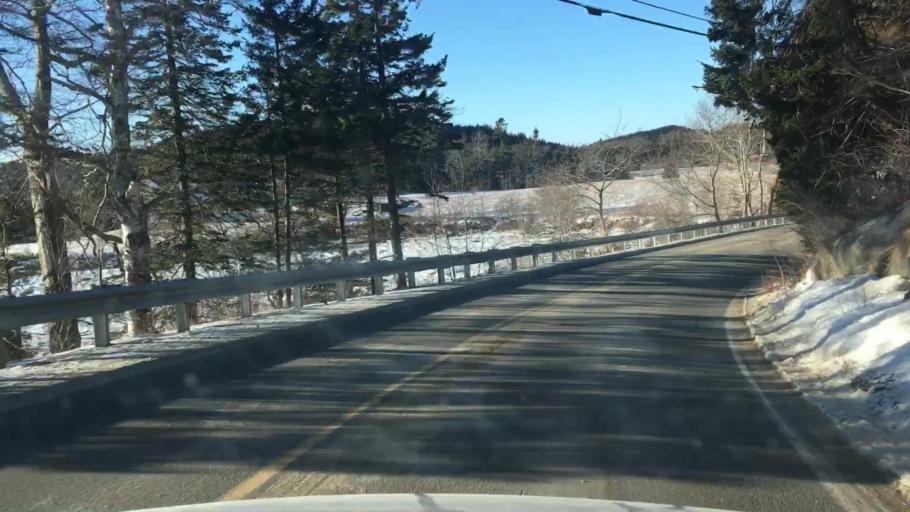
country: US
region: Maine
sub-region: Hancock County
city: Castine
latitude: 44.3493
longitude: -68.7487
